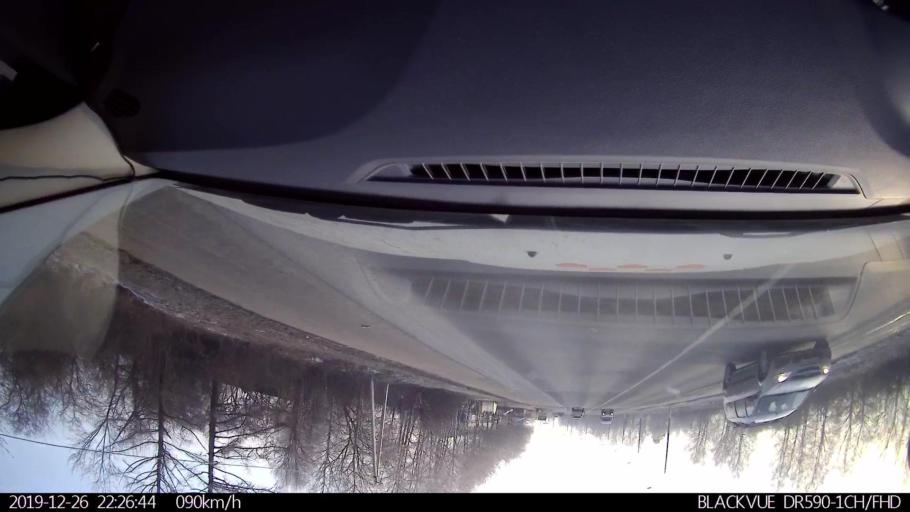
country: RU
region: Nizjnij Novgorod
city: Burevestnik
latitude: 56.1868
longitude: 43.8231
